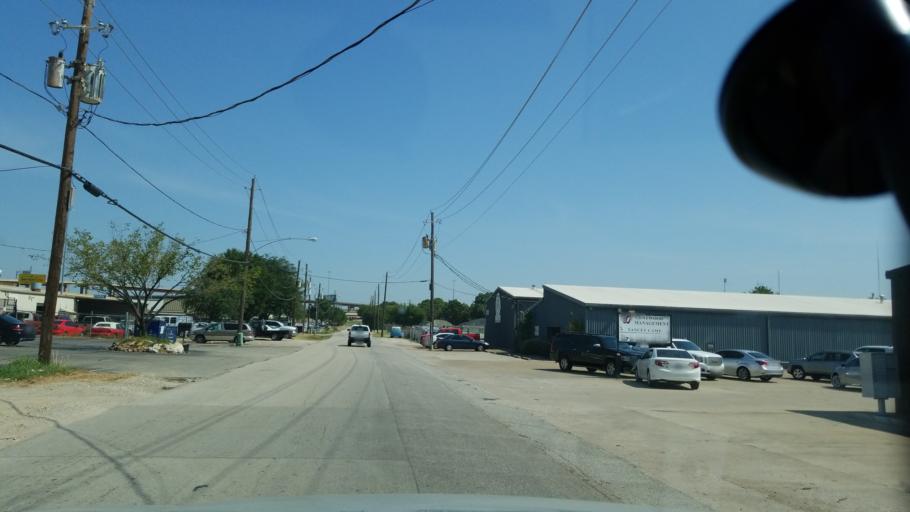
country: US
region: Texas
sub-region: Dallas County
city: Farmers Branch
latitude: 32.9006
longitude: -96.8959
